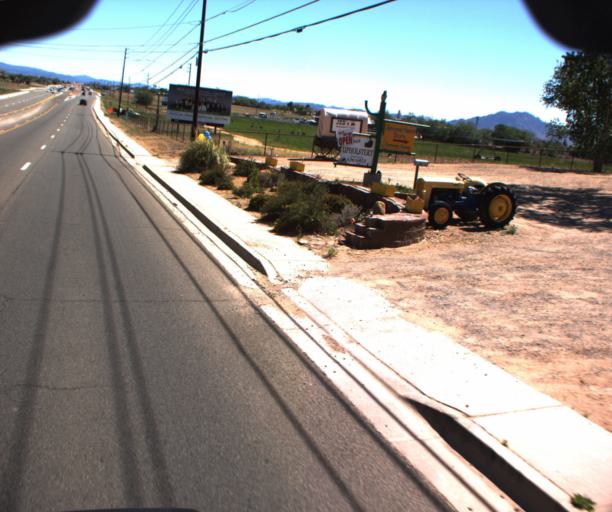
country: US
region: Arizona
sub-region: Yavapai County
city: Chino Valley
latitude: 34.7436
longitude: -112.4547
